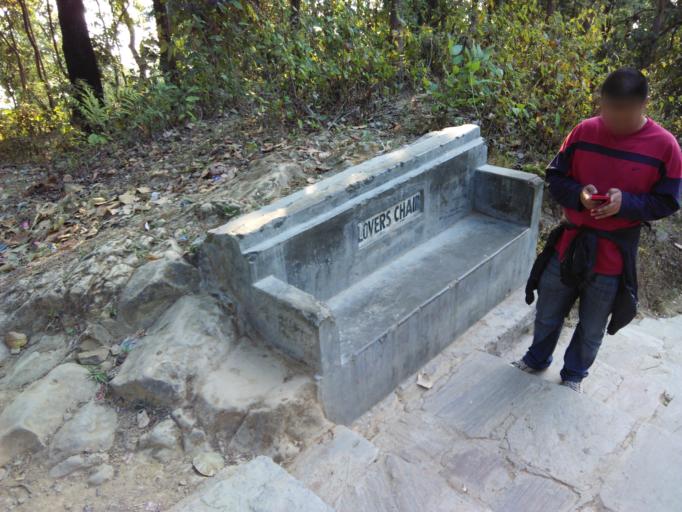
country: NP
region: Central Region
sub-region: Narayani Zone
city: Bharatpur
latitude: 27.7243
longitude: 84.4165
